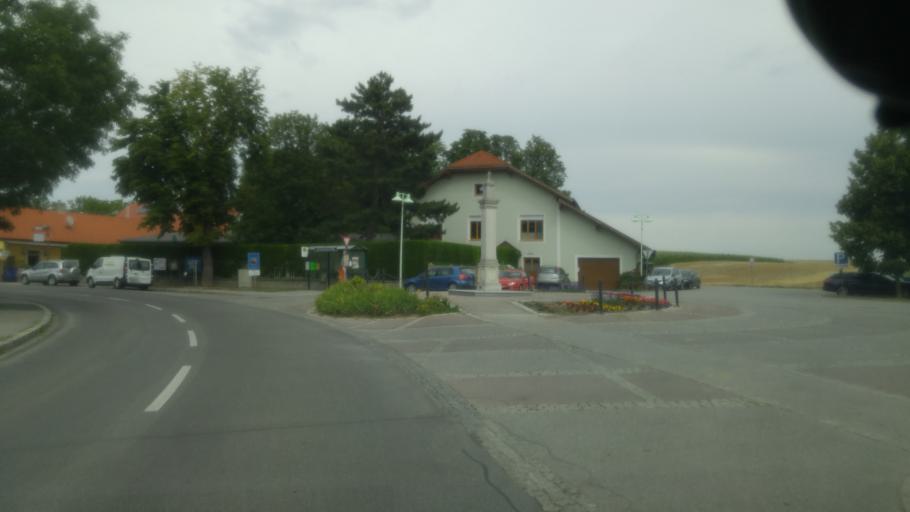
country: AT
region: Lower Austria
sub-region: Politischer Bezirk Wien-Umgebung
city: Moosbrunn
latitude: 48.0398
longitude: 16.4445
